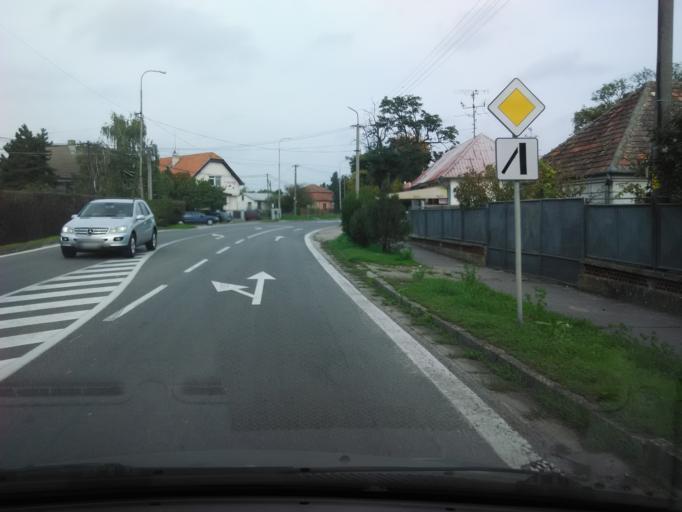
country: SK
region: Nitriansky
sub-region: Okres Komarno
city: Hurbanovo
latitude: 47.8527
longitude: 18.1721
